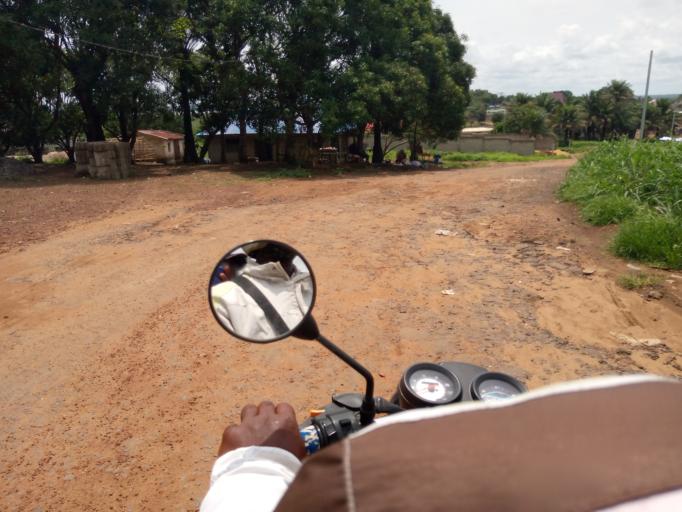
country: SL
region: Western Area
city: Waterloo
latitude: 8.3729
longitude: -13.0880
